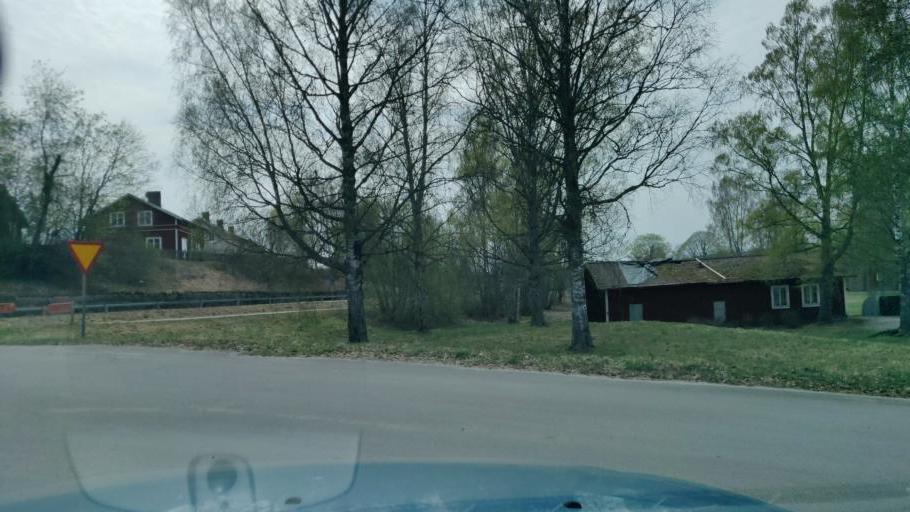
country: SE
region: Vaermland
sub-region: Munkfors Kommun
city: Munkfors
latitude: 59.8451
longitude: 13.5461
